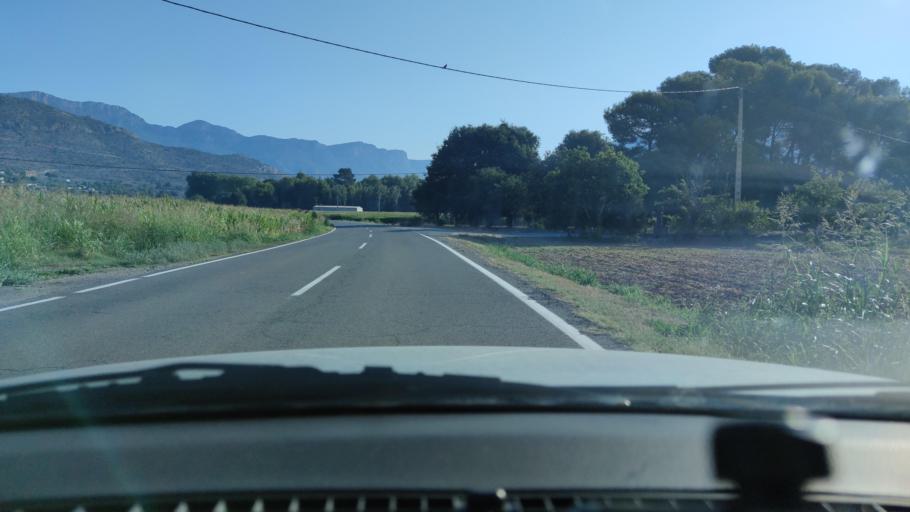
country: ES
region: Catalonia
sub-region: Provincia de Lleida
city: Camarasa
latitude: 41.8547
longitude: 0.8312
